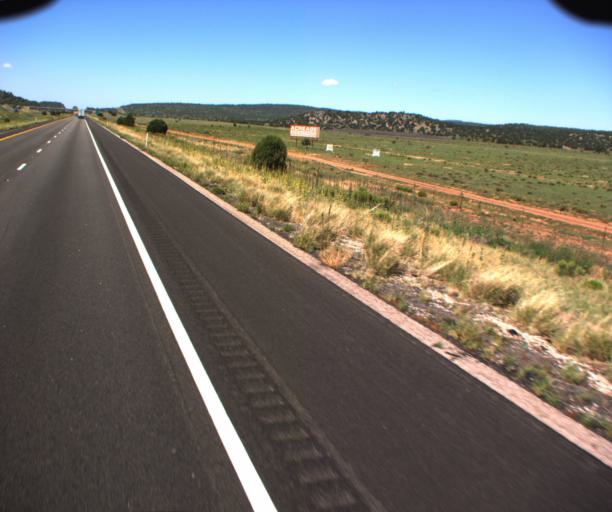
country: US
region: Arizona
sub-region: Mohave County
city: Peach Springs
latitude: 35.2575
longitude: -113.1695
